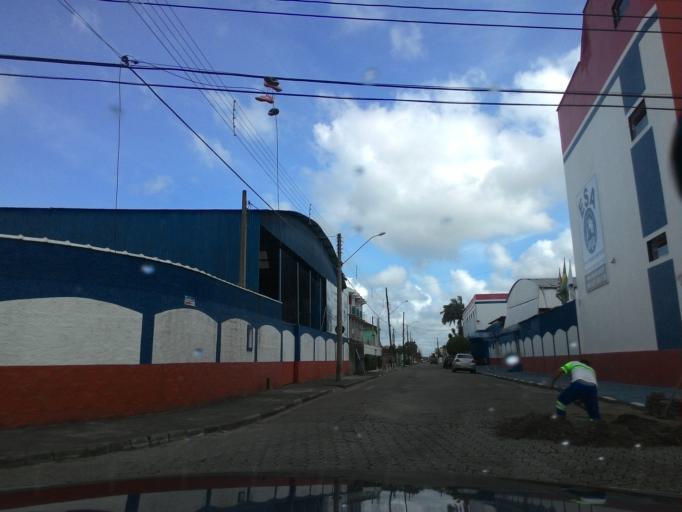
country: BR
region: Sao Paulo
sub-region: Iguape
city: Iguape
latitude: -24.7012
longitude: -47.5598
